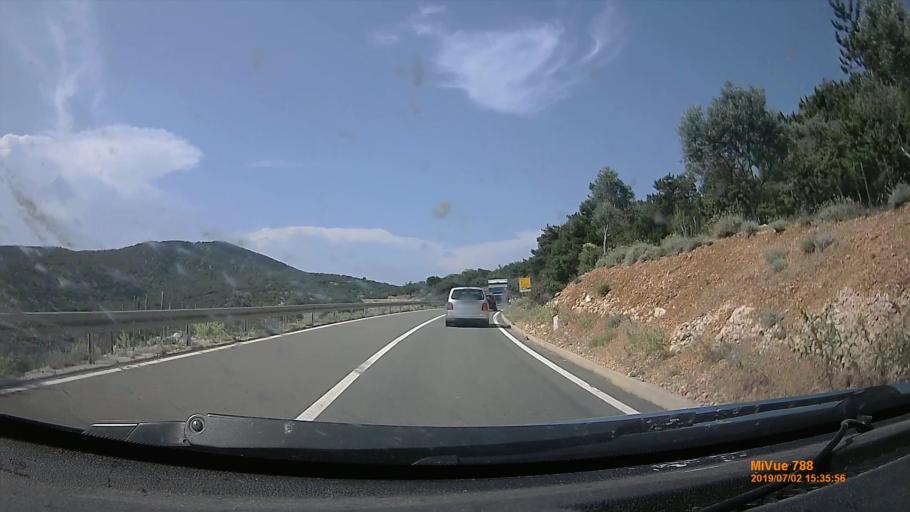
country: HR
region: Primorsko-Goranska
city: Cres
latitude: 44.9808
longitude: 14.4112
